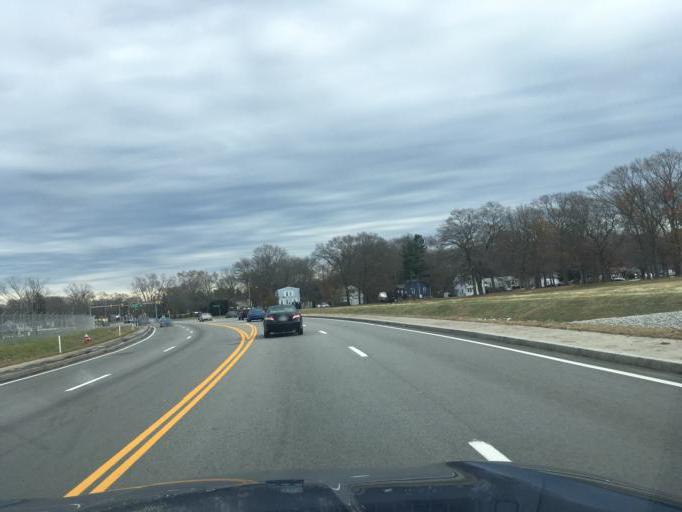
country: US
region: Rhode Island
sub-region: Kent County
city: Warwick
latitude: 41.7077
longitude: -71.4385
